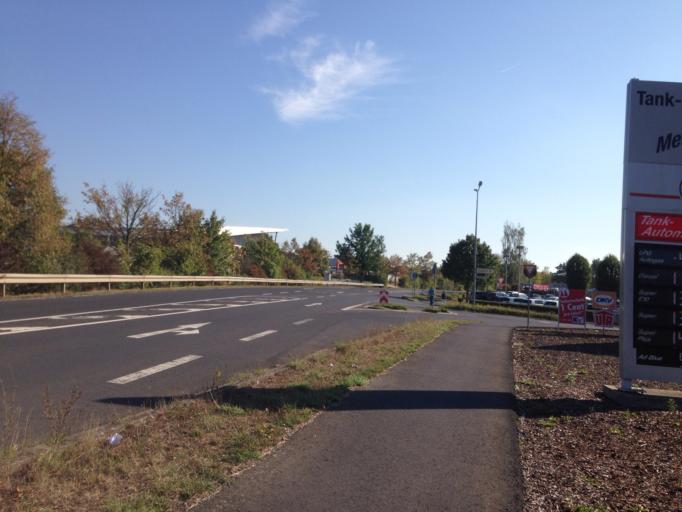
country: DE
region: Hesse
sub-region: Regierungsbezirk Giessen
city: Giessen
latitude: 50.5428
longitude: 8.7063
